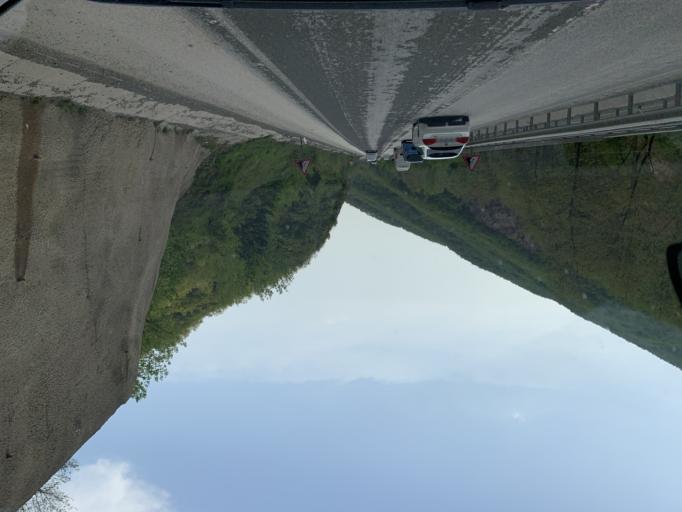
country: TR
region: Bursa
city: Kursunlu
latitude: 39.9993
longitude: 29.6531
